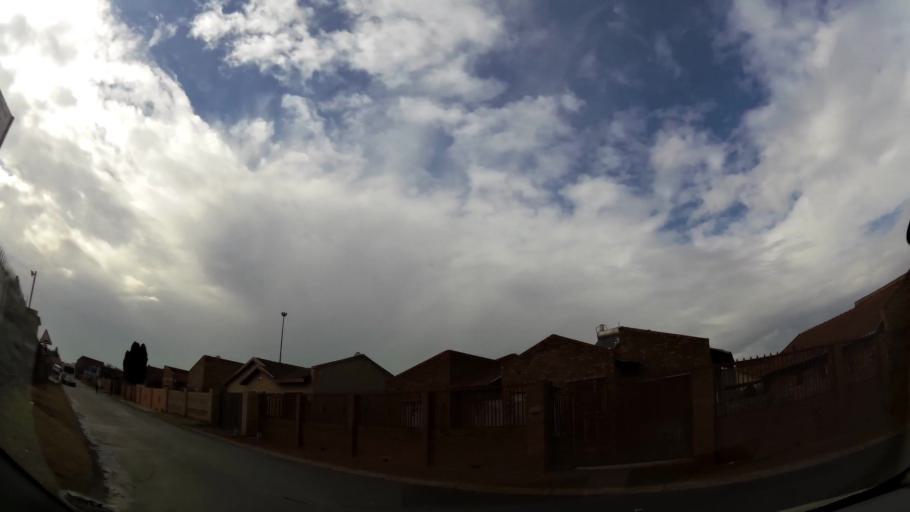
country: ZA
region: Gauteng
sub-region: Ekurhuleni Metropolitan Municipality
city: Germiston
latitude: -26.3286
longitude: 28.1819
